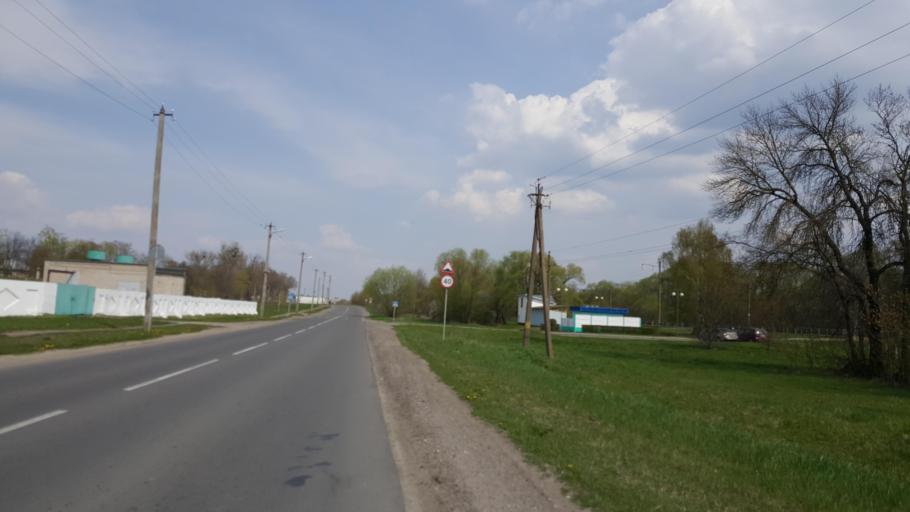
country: BY
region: Brest
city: Zhabinka
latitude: 52.1879
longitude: 23.9817
